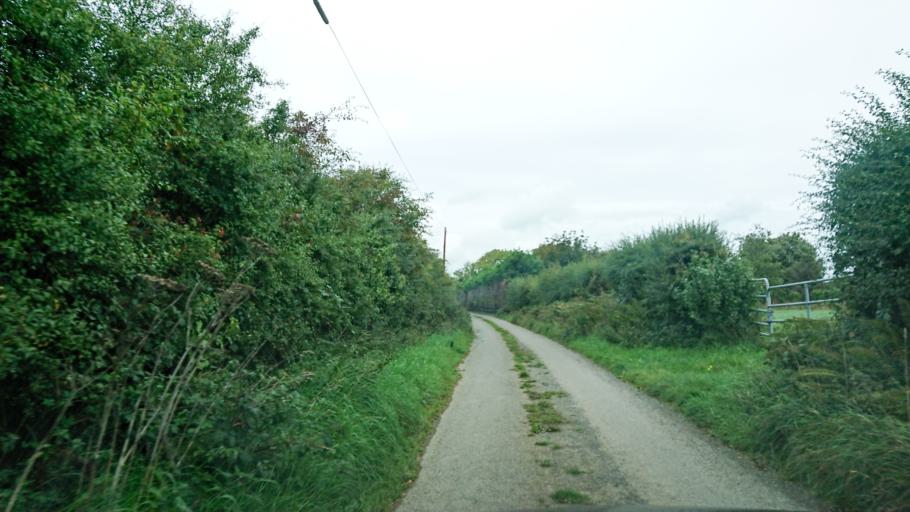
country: IE
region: Munster
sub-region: Waterford
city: Dunmore East
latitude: 52.2084
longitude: -7.0432
